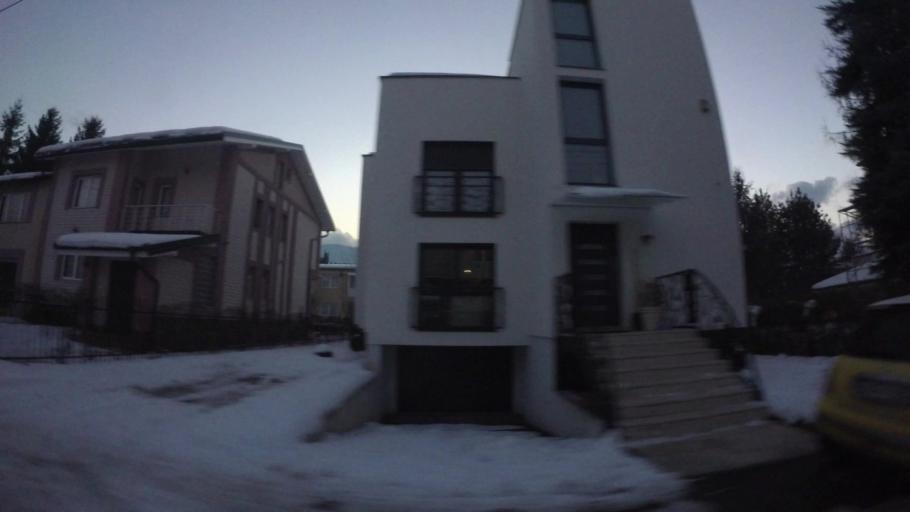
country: BA
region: Federation of Bosnia and Herzegovina
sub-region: Kanton Sarajevo
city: Sarajevo
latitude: 43.8284
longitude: 18.2997
